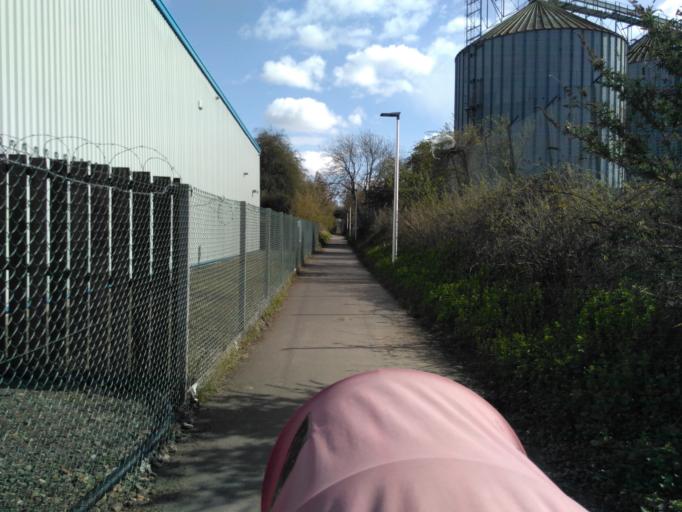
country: GB
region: Scotland
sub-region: Midlothian
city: Loanhead
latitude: 55.8860
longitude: -3.1470
